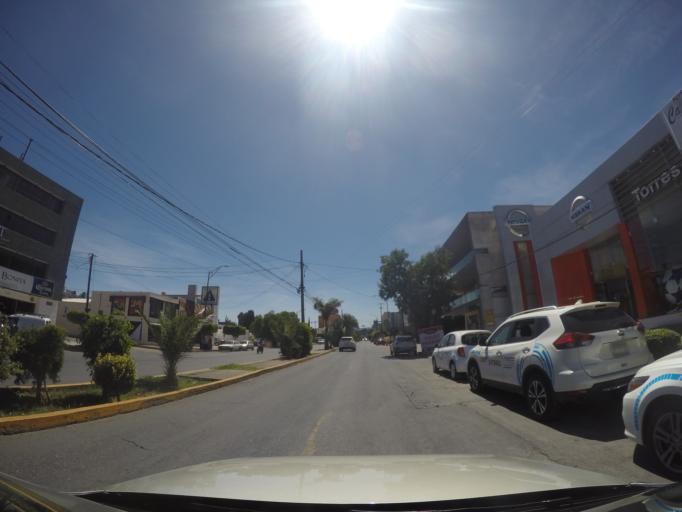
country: MX
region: San Luis Potosi
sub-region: San Luis Potosi
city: San Luis Potosi
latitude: 22.1490
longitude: -101.0089
